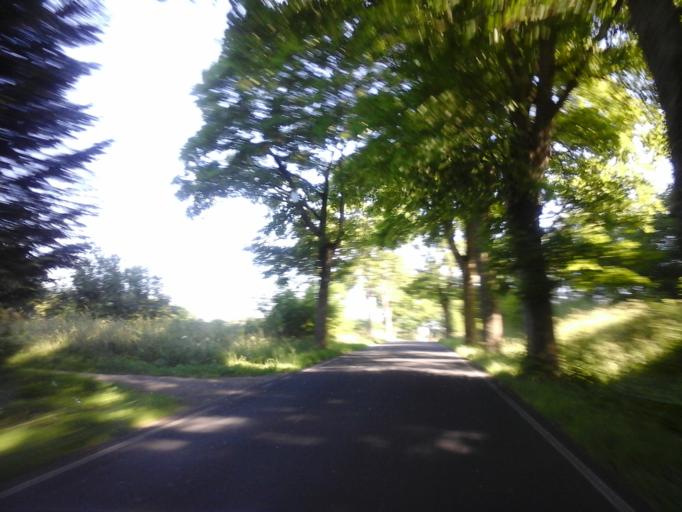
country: PL
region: West Pomeranian Voivodeship
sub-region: Powiat drawski
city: Zlocieniec
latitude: 53.6175
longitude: 15.9227
